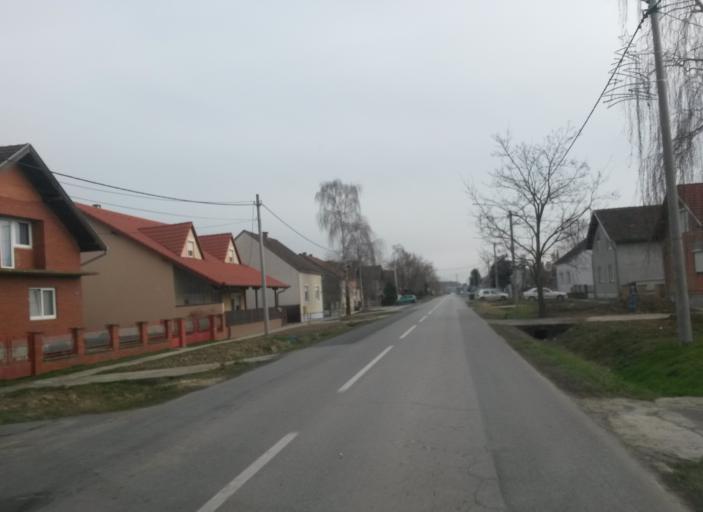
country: HR
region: Osjecko-Baranjska
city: Antunovac
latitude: 45.4784
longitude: 18.6524
